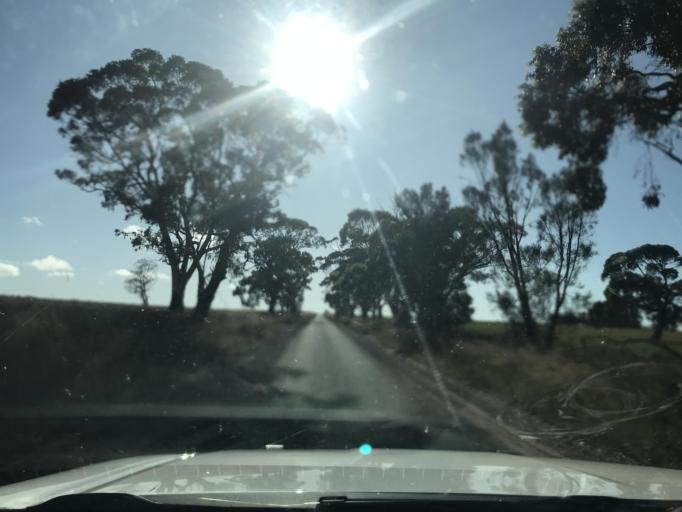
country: AU
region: Victoria
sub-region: Horsham
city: Horsham
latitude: -36.6951
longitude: 141.5753
